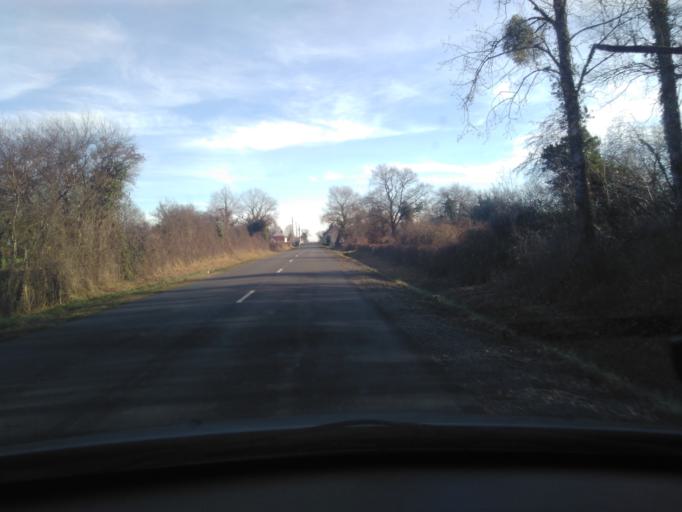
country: FR
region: Centre
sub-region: Departement du Cher
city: Orval
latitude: 46.6541
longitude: 2.4104
